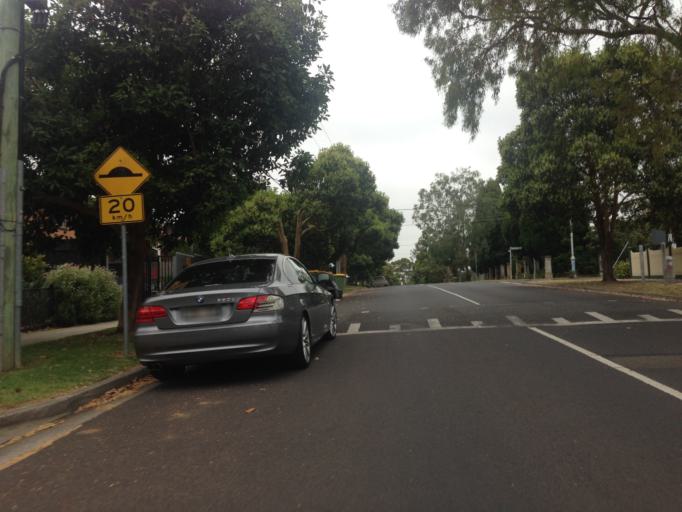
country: AU
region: Victoria
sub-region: Darebin
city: Thornbury
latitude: -37.7519
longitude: 145.0065
